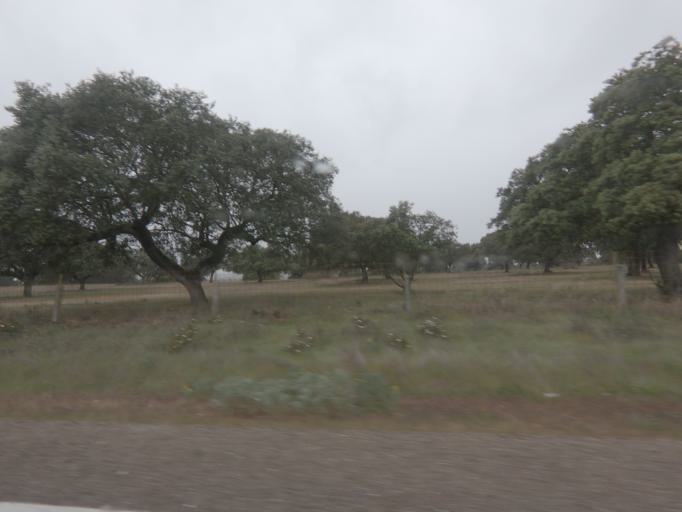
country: ES
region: Extremadura
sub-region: Provincia de Badajoz
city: Badajoz
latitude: 38.9513
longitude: -6.9114
